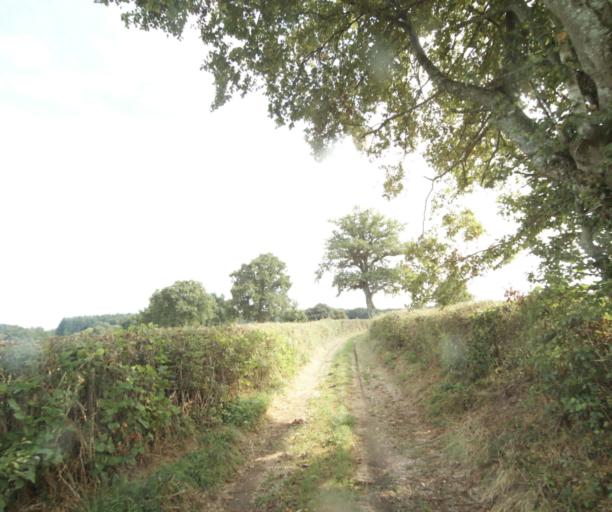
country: FR
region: Bourgogne
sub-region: Departement de Saone-et-Loire
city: Palinges
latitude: 46.5127
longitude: 4.2688
